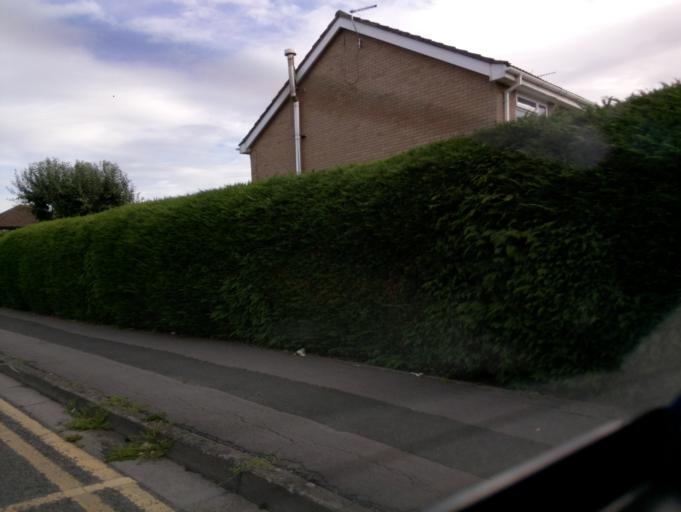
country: GB
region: England
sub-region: Gloucestershire
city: Gloucester
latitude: 51.8253
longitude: -2.2818
